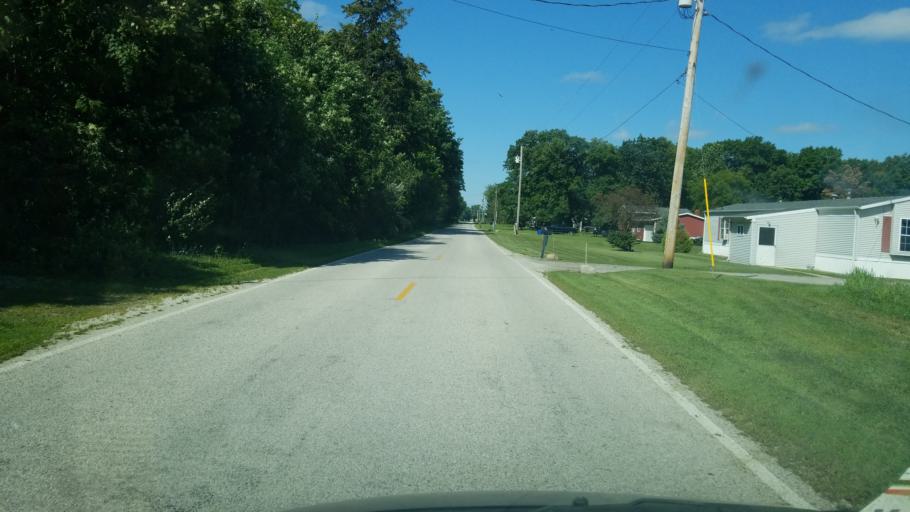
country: US
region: Ohio
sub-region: Wood County
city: North Baltimore
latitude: 41.1242
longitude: -83.6614
